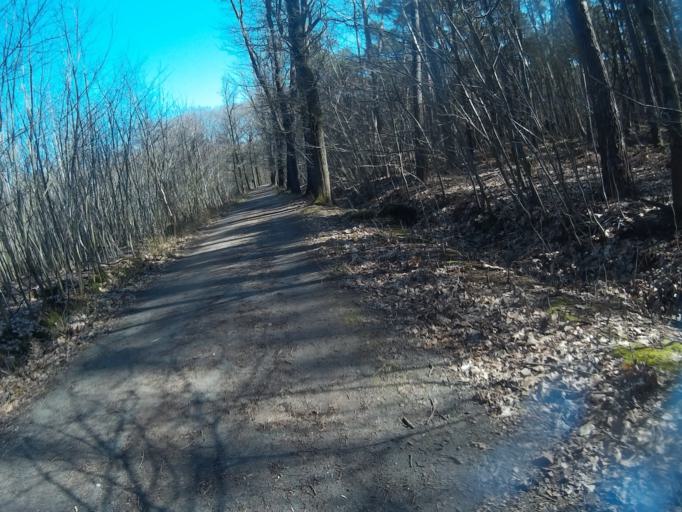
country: BE
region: Flanders
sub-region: Provincie Oost-Vlaanderen
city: Knesselare
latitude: 51.1469
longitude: 3.4552
